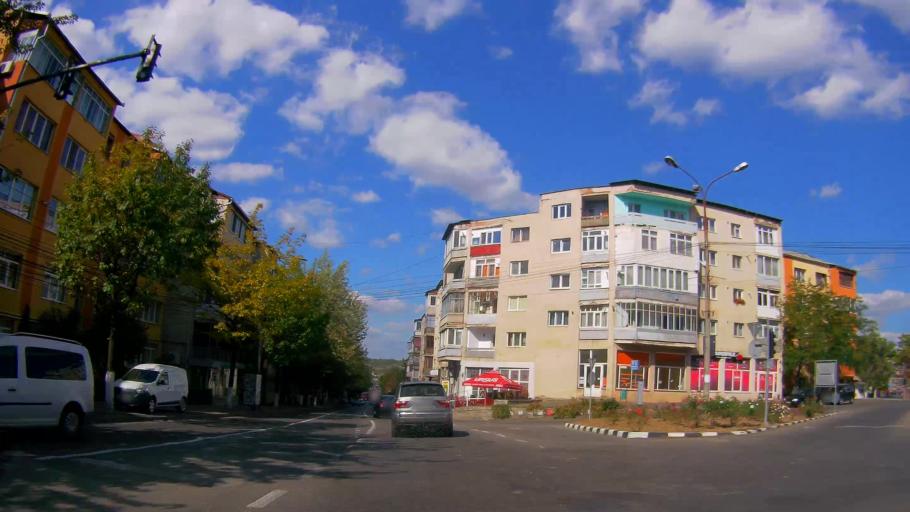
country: RO
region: Salaj
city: Zalau
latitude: 47.1888
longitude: 23.0619
